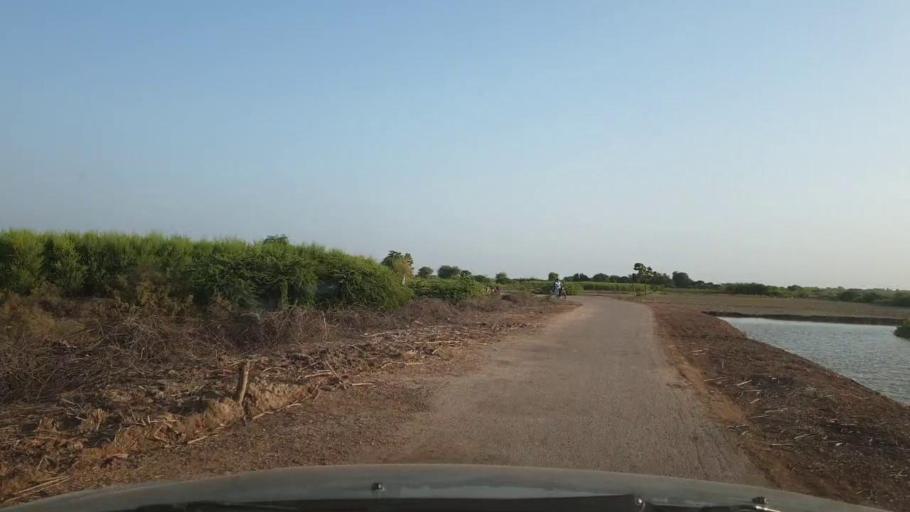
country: PK
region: Sindh
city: Tando Ghulam Ali
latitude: 25.1229
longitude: 68.9645
